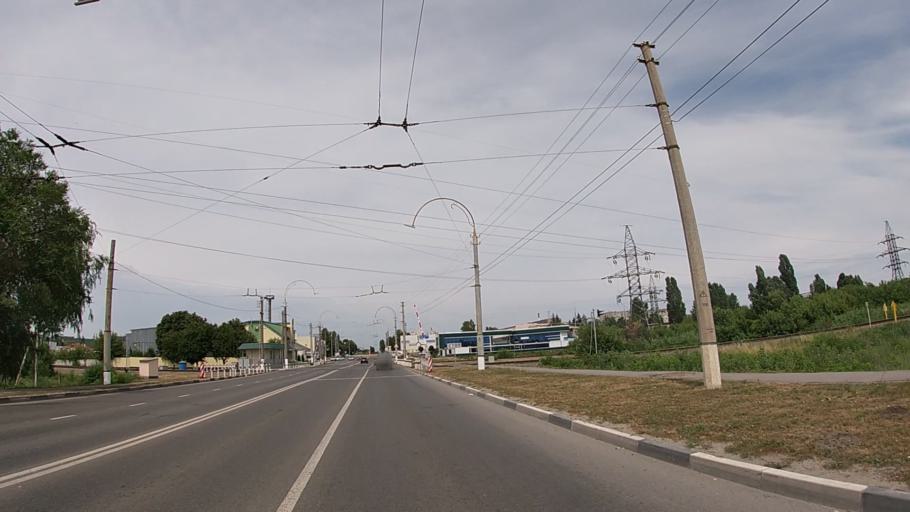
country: RU
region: Belgorod
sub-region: Belgorodskiy Rayon
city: Belgorod
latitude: 50.6120
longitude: 36.5387
